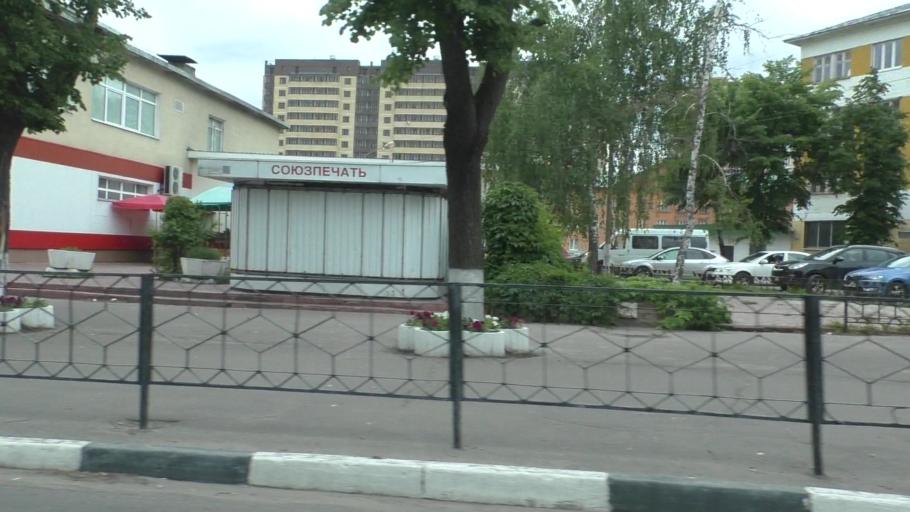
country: RU
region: Moskovskaya
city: Yegor'yevsk
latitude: 55.3755
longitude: 39.0475
